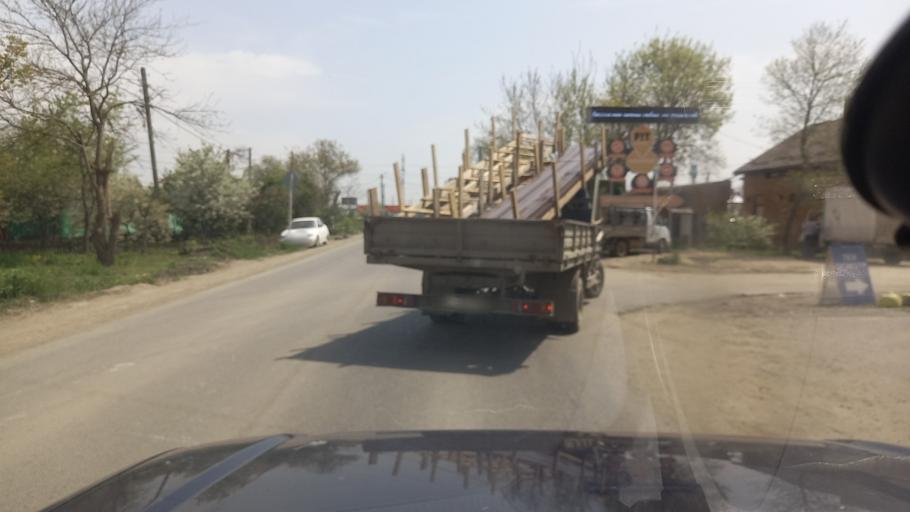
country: RU
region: Adygeya
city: Yablonovskiy
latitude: 44.9865
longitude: 38.9620
